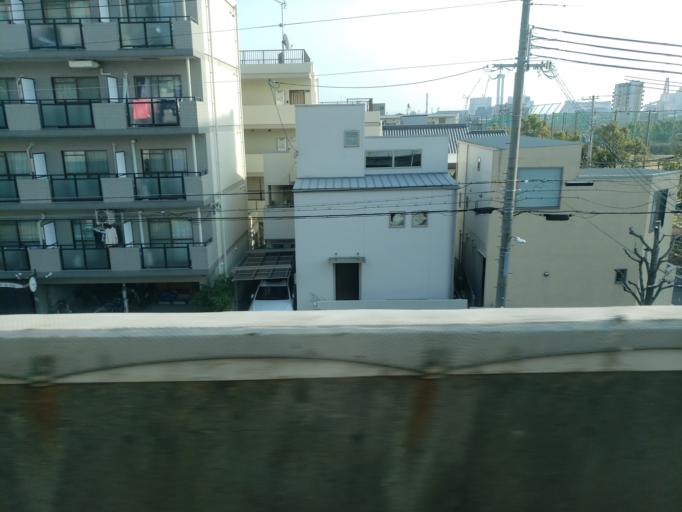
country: JP
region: Hyogo
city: Ashiya
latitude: 34.7178
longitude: 135.2433
